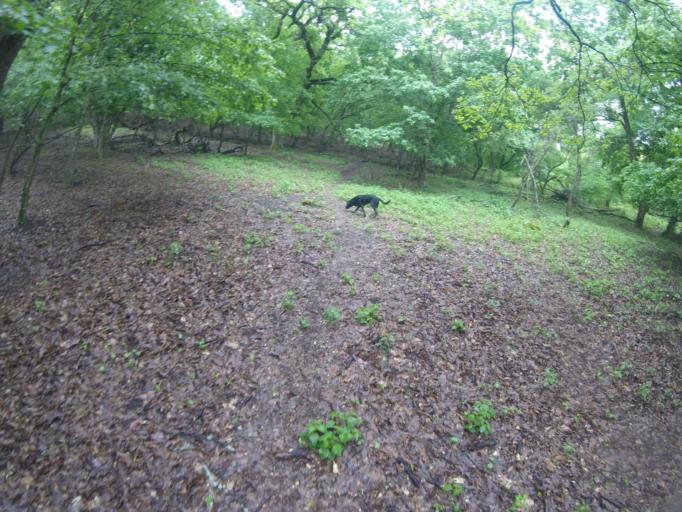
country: HU
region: Nograd
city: Matraverebely
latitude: 47.9980
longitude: 19.7530
